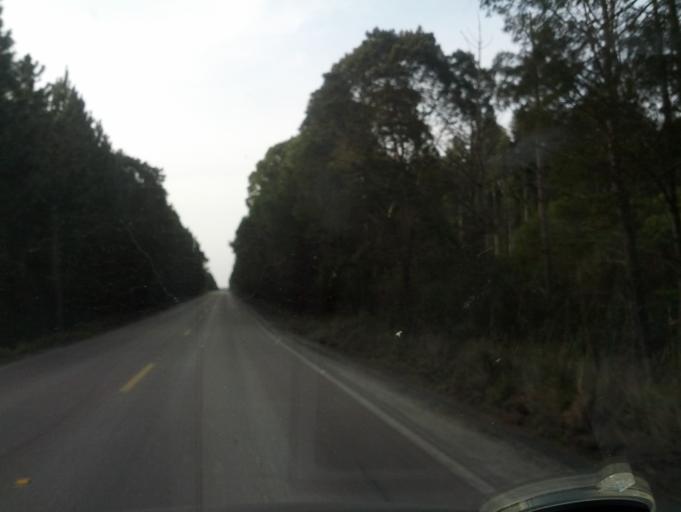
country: BR
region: Santa Catarina
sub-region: Otacilio Costa
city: Otacilio Costa
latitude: -27.3779
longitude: -50.1345
